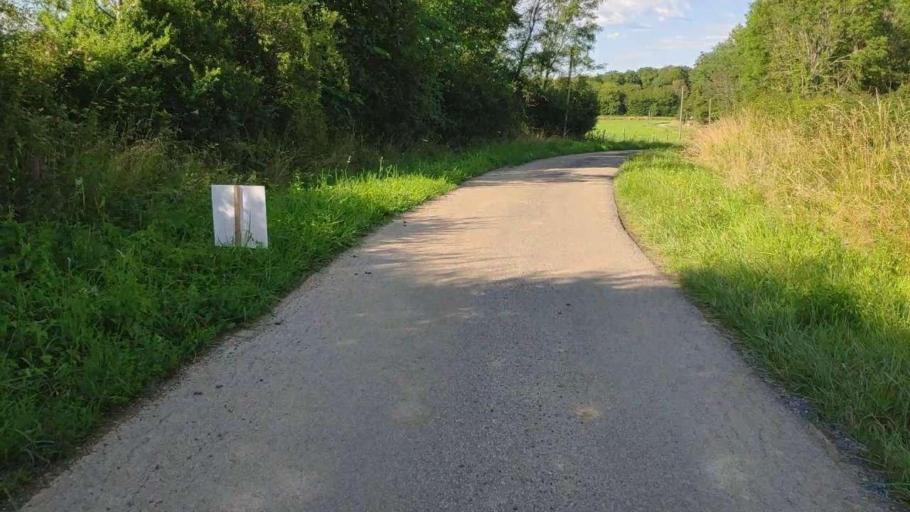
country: FR
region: Franche-Comte
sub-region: Departement du Jura
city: Bletterans
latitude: 46.8333
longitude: 5.5021
